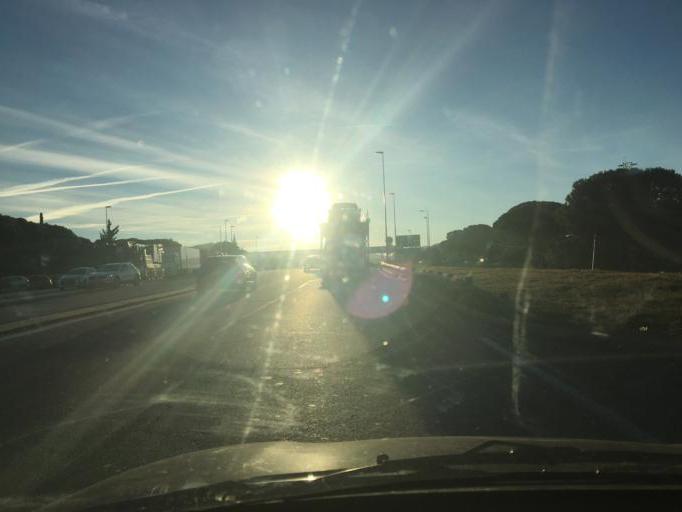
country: FR
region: Provence-Alpes-Cote d'Azur
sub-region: Departement du Var
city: Le Muy
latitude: 43.4619
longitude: 6.5490
